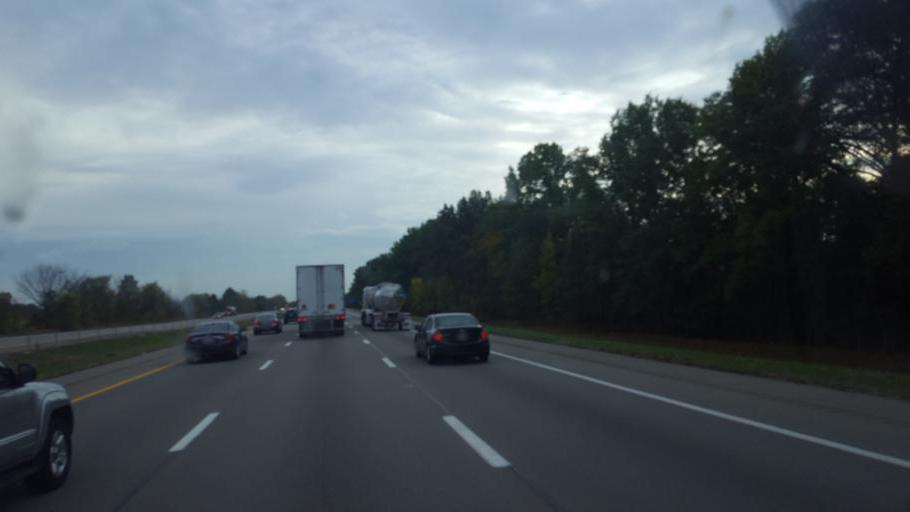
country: US
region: Ohio
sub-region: Delaware County
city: Sunbury
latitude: 40.2937
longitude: -82.9250
